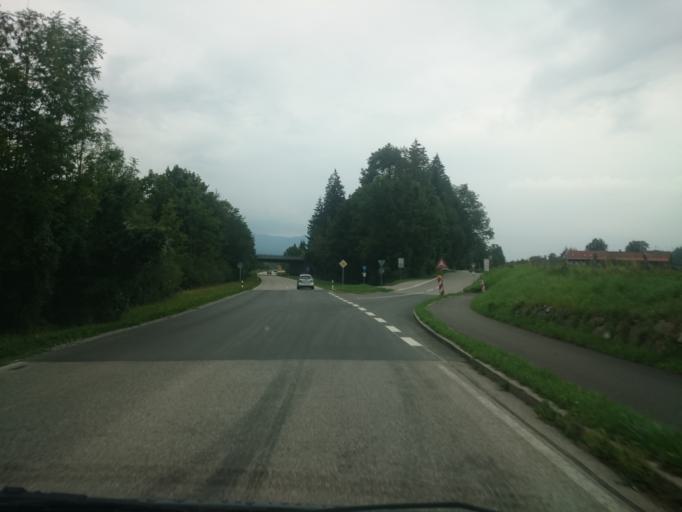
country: DE
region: Bavaria
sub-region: Upper Bavaria
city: Lenggries
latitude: 47.6576
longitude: 11.5882
